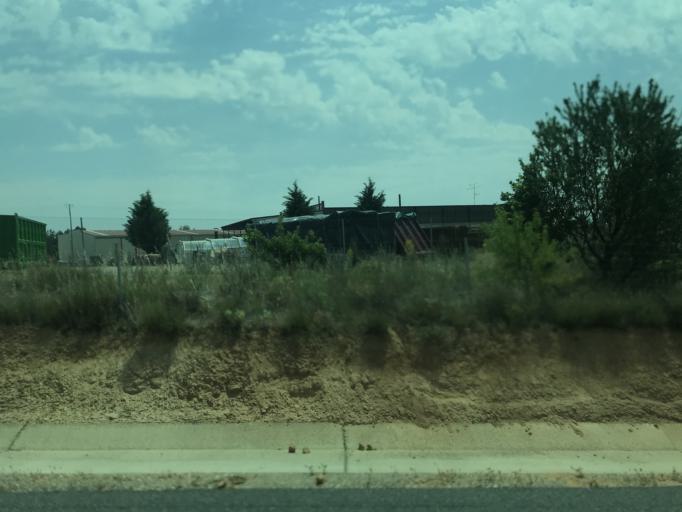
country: ES
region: Castille and Leon
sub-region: Provincia de Burgos
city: Oquillas
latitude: 41.7768
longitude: -3.6971
